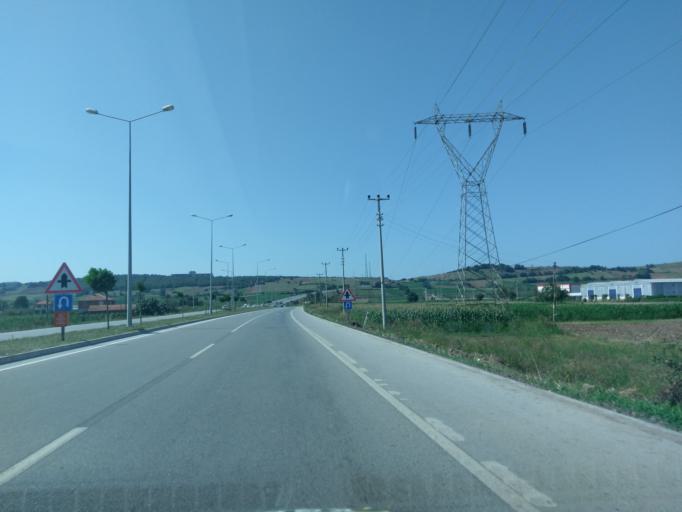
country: TR
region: Samsun
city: Bafra
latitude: 41.5771
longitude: 35.8548
